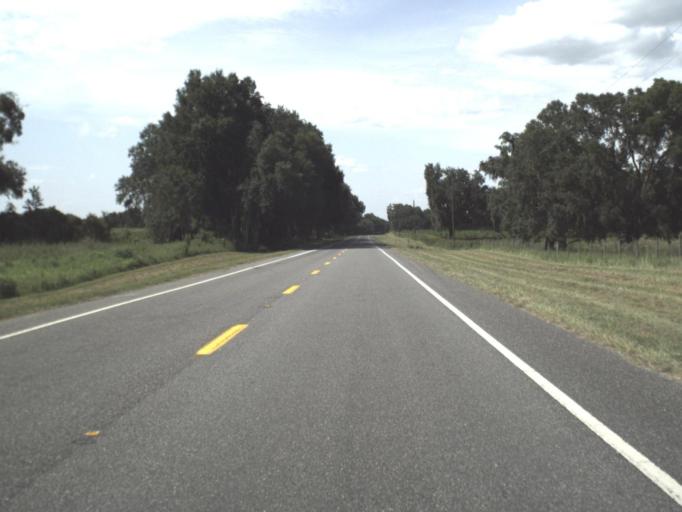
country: US
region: Florida
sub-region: Alachua County
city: High Springs
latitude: 29.9459
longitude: -82.7134
